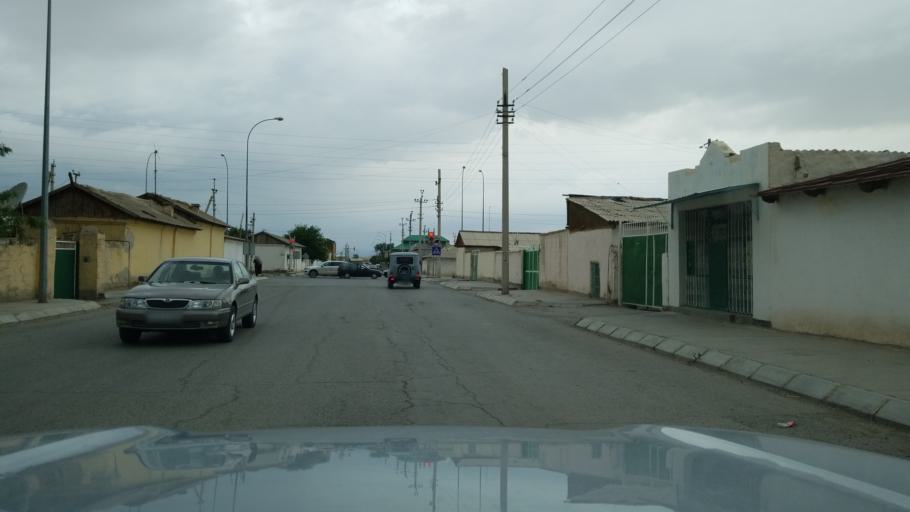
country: TM
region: Balkan
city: Serdar
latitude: 38.9728
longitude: 56.2803
